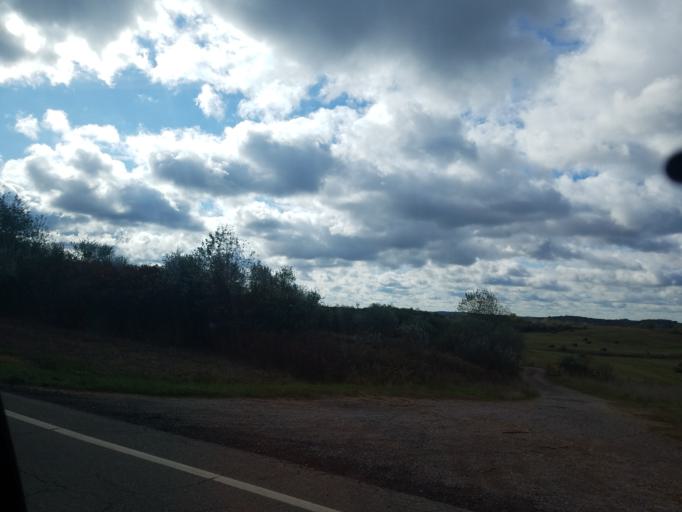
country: US
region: Ohio
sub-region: Vinton County
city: McArthur
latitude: 39.1774
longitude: -82.4523
